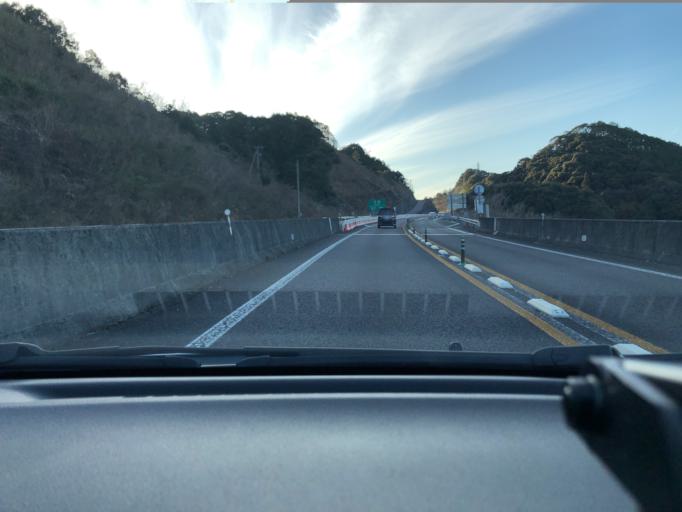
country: JP
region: Kochi
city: Sukumo
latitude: 32.9573
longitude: 132.8282
